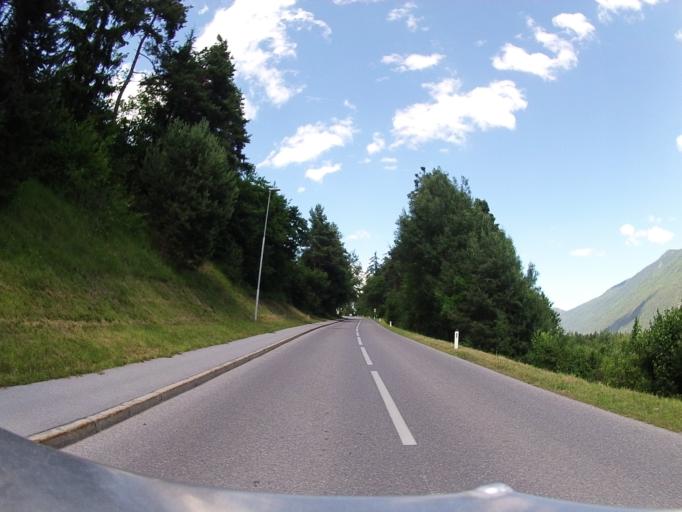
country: AT
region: Tyrol
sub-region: Politischer Bezirk Imst
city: Imst
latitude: 47.2537
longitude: 10.7386
